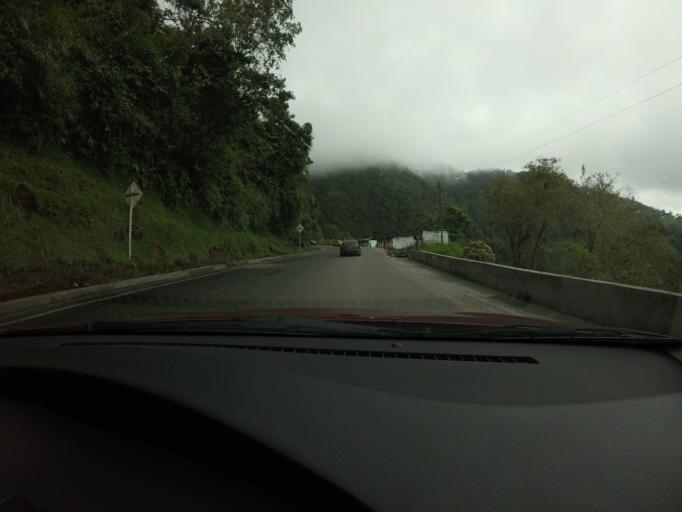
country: CO
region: Tolima
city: Herveo
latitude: 5.1243
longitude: -75.2037
